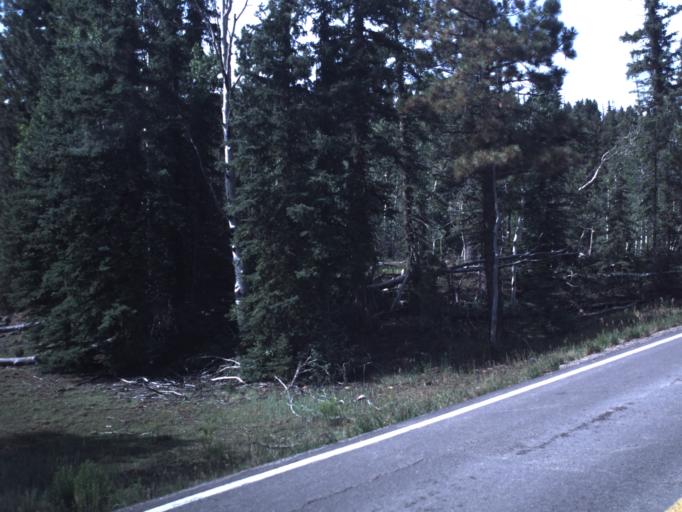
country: US
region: Utah
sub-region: Iron County
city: Parowan
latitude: 37.5202
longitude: -112.6720
